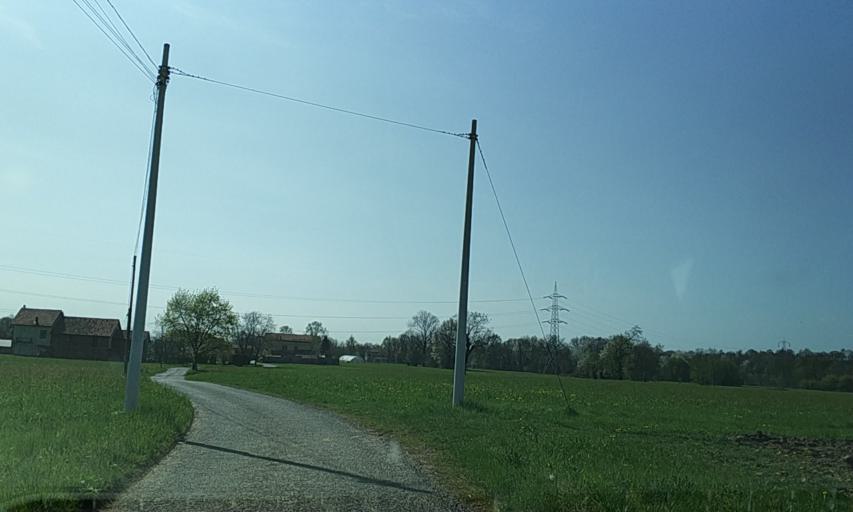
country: IT
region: Piedmont
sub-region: Provincia di Torino
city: Villanova Canavese
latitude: 45.2340
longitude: 7.5361
